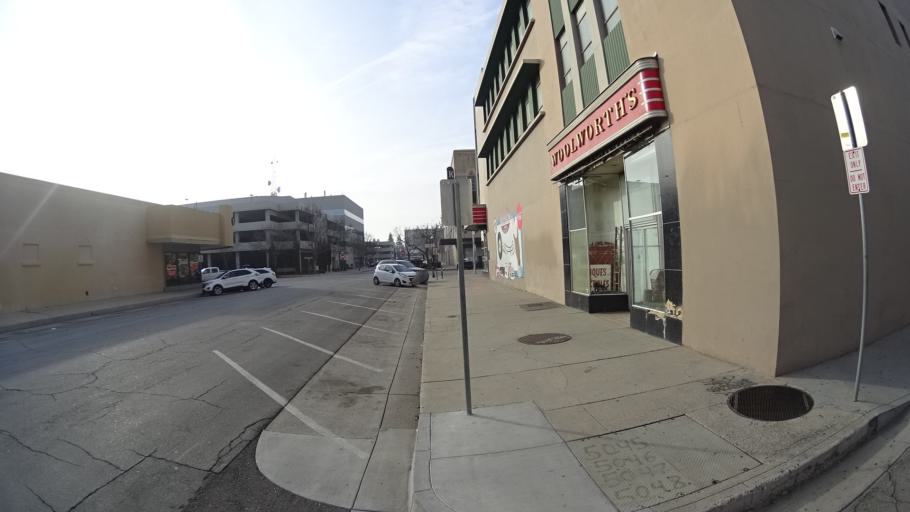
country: US
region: California
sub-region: Kern County
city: Bakersfield
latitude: 35.3767
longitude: -119.0177
